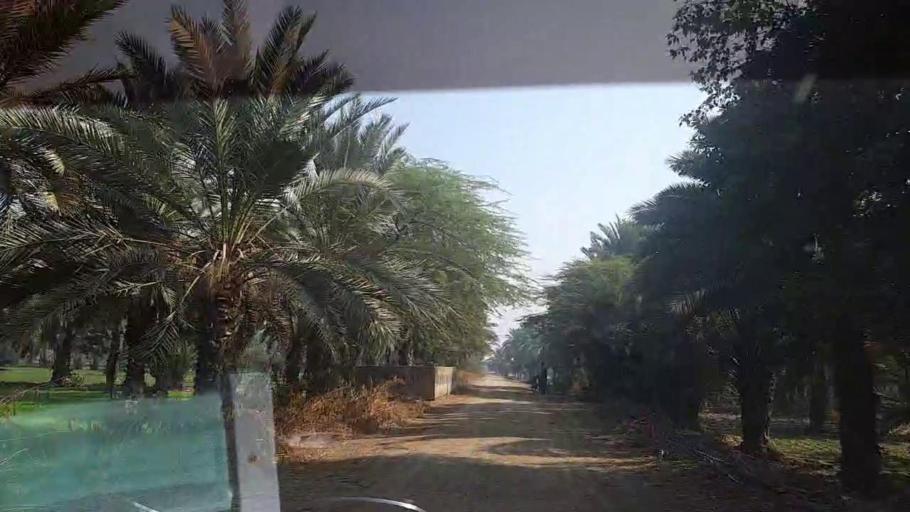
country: PK
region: Sindh
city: Kot Diji
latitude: 27.4333
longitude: 68.6934
